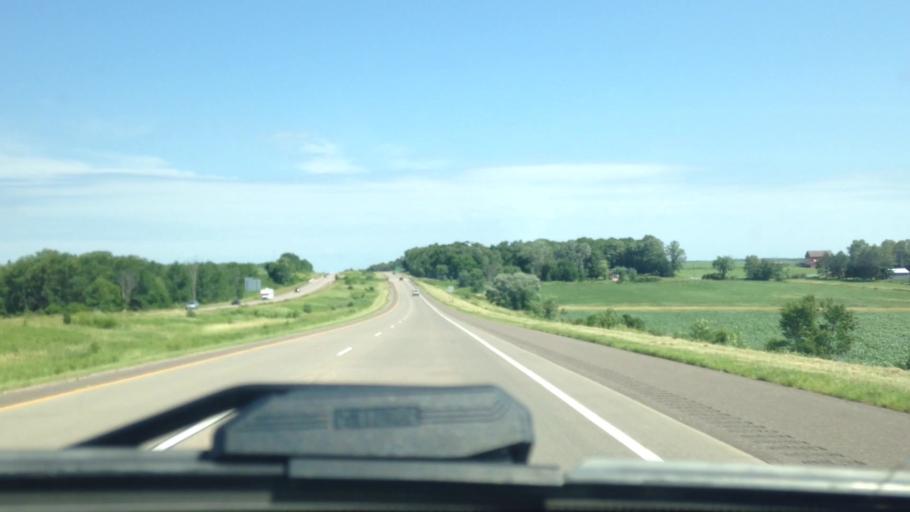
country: US
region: Wisconsin
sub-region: Barron County
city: Rice Lake
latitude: 45.5259
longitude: -91.7594
